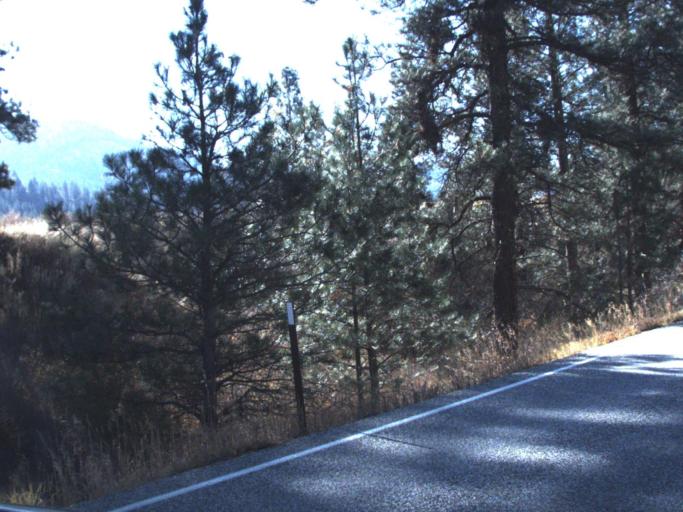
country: US
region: Washington
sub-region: Ferry County
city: Republic
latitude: 48.7993
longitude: -118.6122
